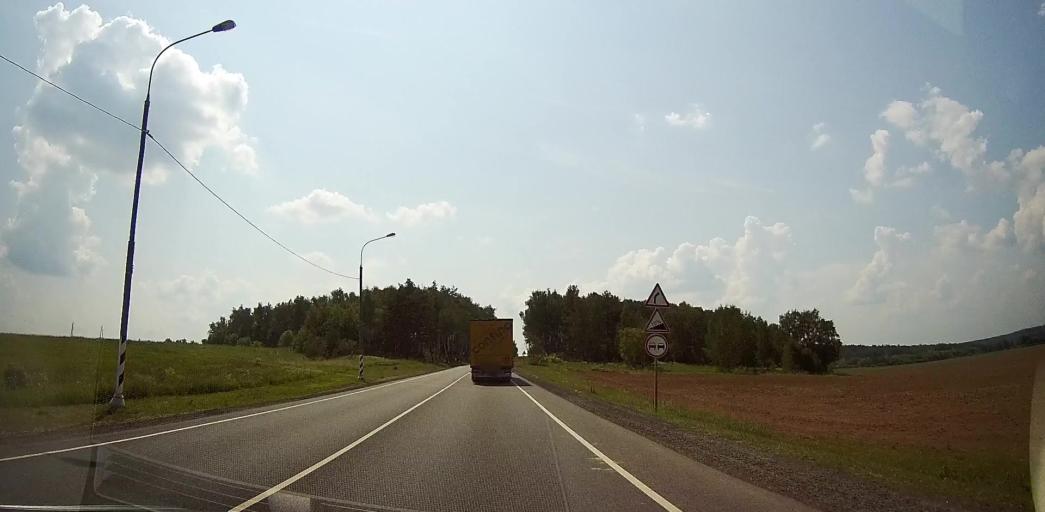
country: RU
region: Moskovskaya
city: Meshcherino
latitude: 55.1835
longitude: 38.3531
